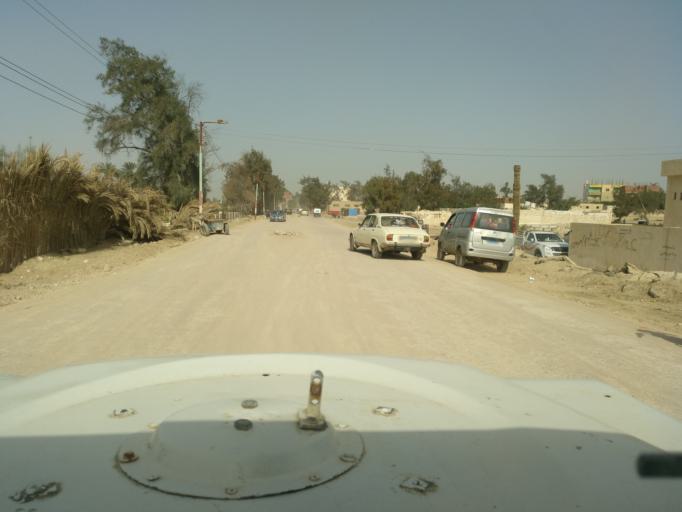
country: EG
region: Al Buhayrah
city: Beheira
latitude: 30.3684
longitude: 30.3586
